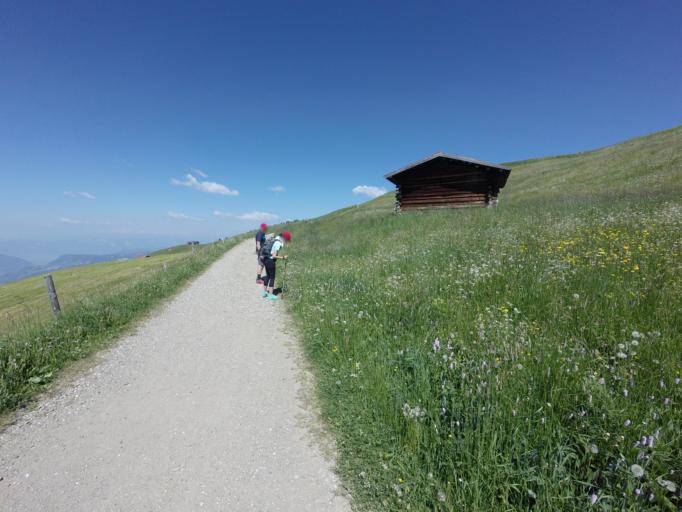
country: IT
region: Trentino-Alto Adige
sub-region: Bolzano
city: Siusi
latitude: 46.5485
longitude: 11.6067
